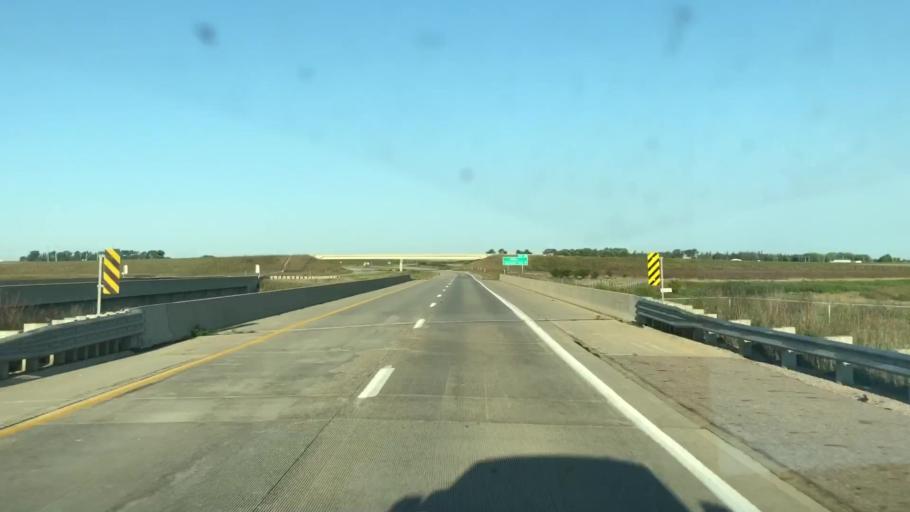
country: US
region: Iowa
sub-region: Osceola County
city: Sibley
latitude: 43.3845
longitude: -95.7367
